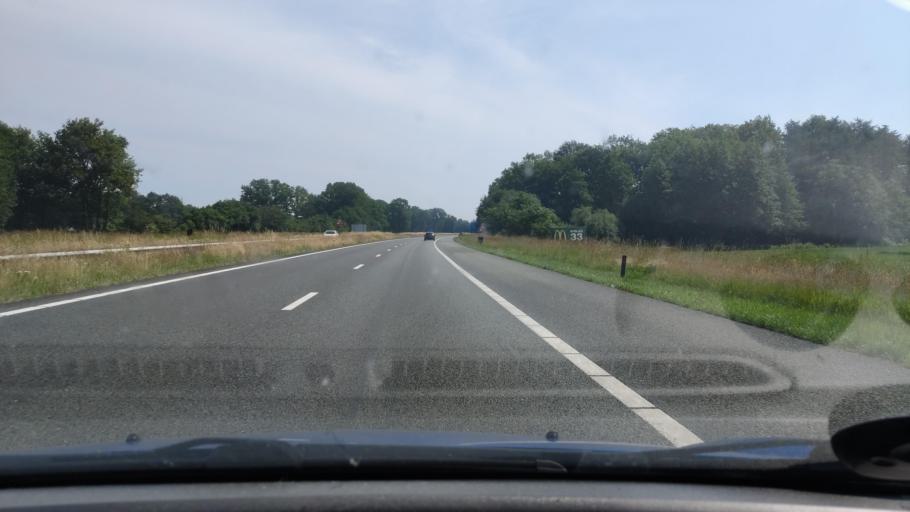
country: NL
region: Overijssel
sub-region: Gemeente Oldenzaal
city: Oldenzaal
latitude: 52.2917
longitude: 6.8742
